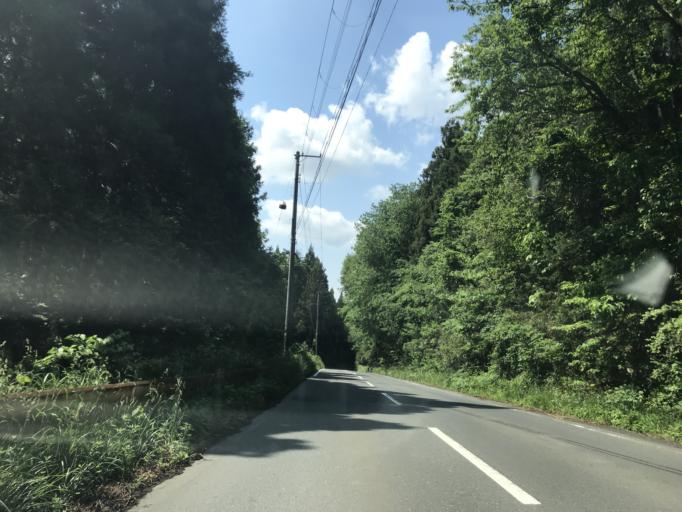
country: JP
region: Miyagi
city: Furukawa
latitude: 38.7124
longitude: 140.9421
